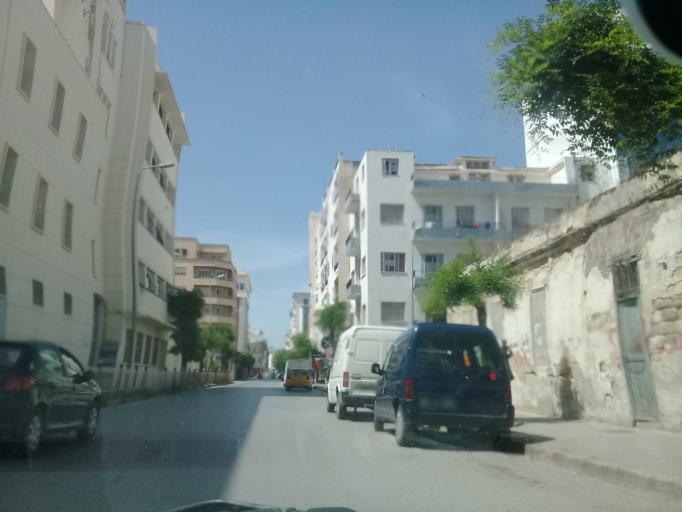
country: TN
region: Tunis
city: Tunis
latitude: 36.8136
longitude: 10.1803
